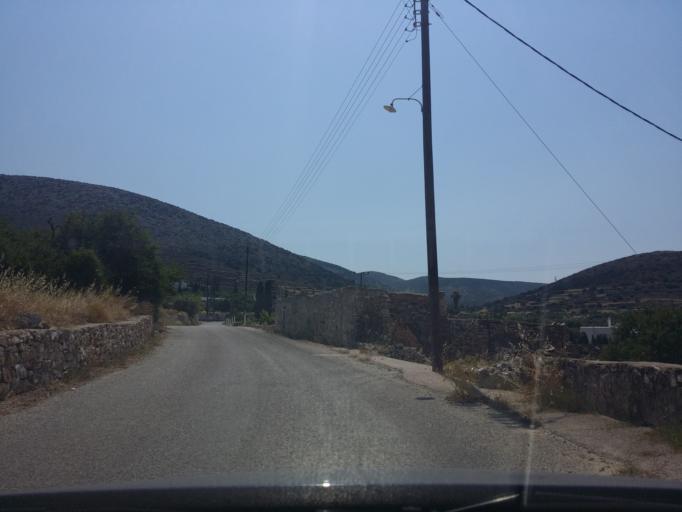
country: GR
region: South Aegean
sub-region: Nomos Kykladon
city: Antiparos
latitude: 37.0148
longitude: 25.1454
